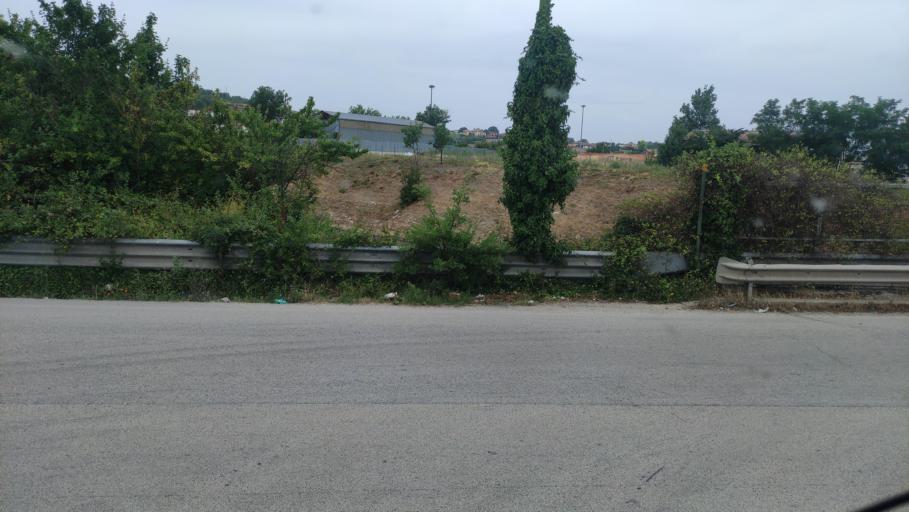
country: IT
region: Campania
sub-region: Provincia di Avellino
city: Grottaminarda
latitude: 41.0633
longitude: 15.0581
